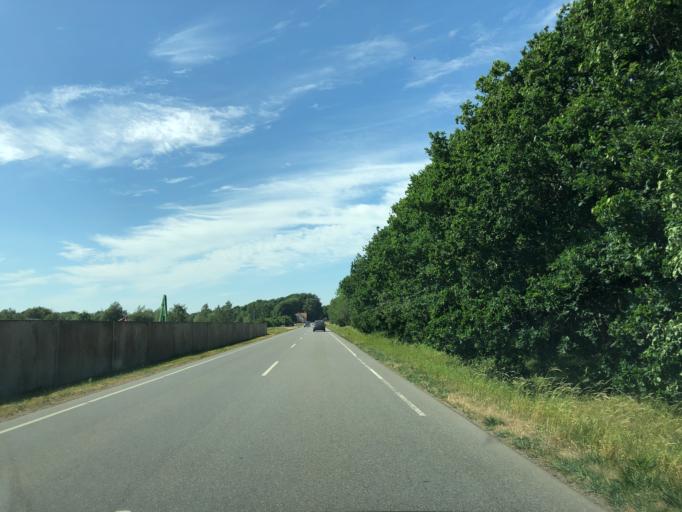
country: DK
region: Central Jutland
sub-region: Ikast-Brande Kommune
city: Brande
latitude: 55.9298
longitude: 9.1499
